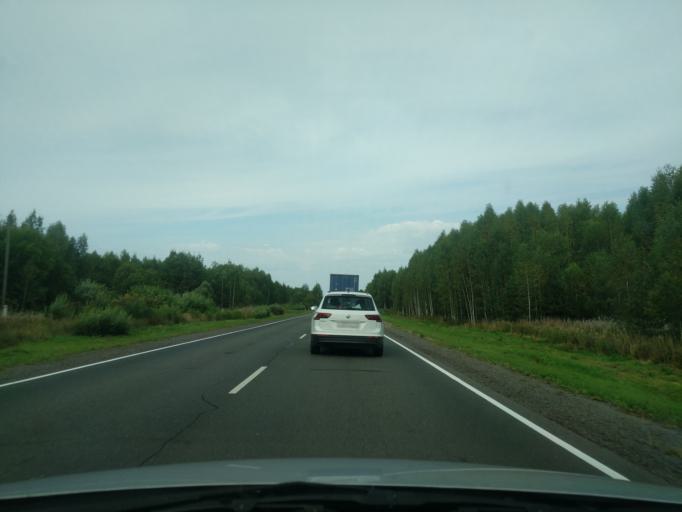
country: RU
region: Kirov
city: Leninskoye
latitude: 58.2850
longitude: 47.2505
